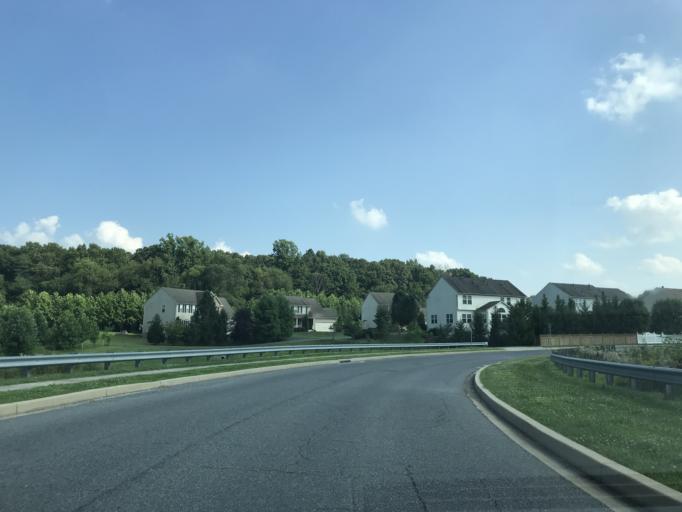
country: US
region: Maryland
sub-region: Carroll County
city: Manchester
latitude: 39.6807
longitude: -76.8879
